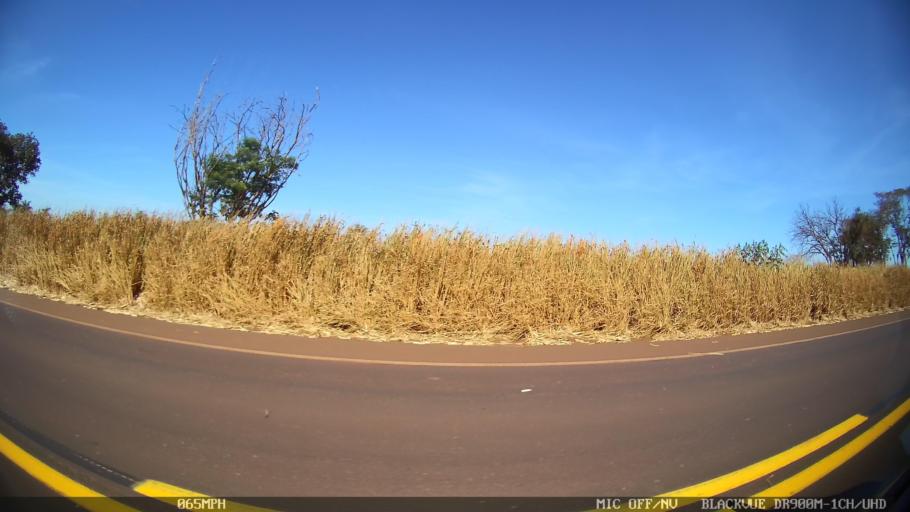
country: BR
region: Sao Paulo
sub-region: Barretos
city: Barretos
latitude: -20.4616
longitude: -48.4683
